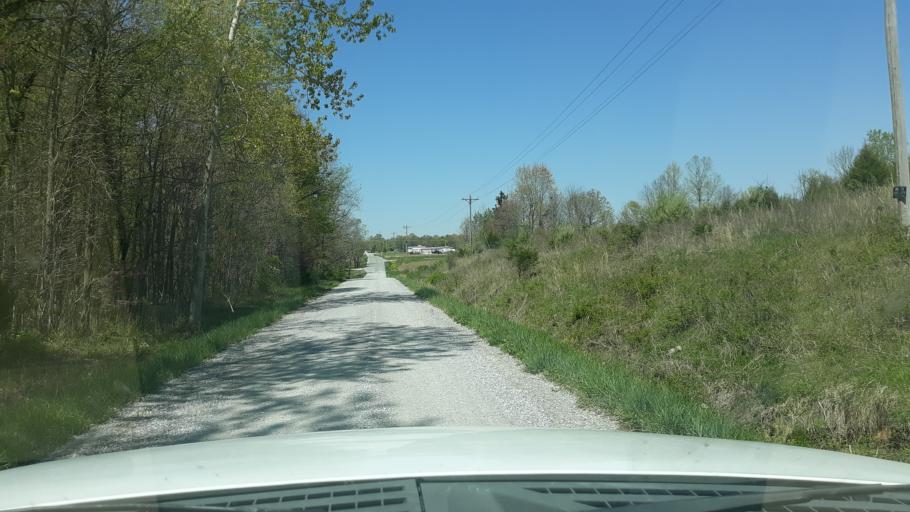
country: US
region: Illinois
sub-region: Saline County
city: Harrisburg
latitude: 37.8724
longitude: -88.6422
